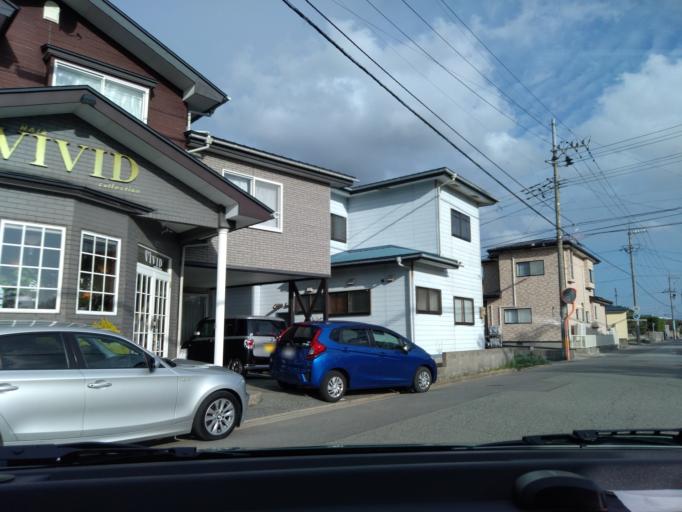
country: JP
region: Akita
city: Akita Shi
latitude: 39.7715
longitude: 140.0817
